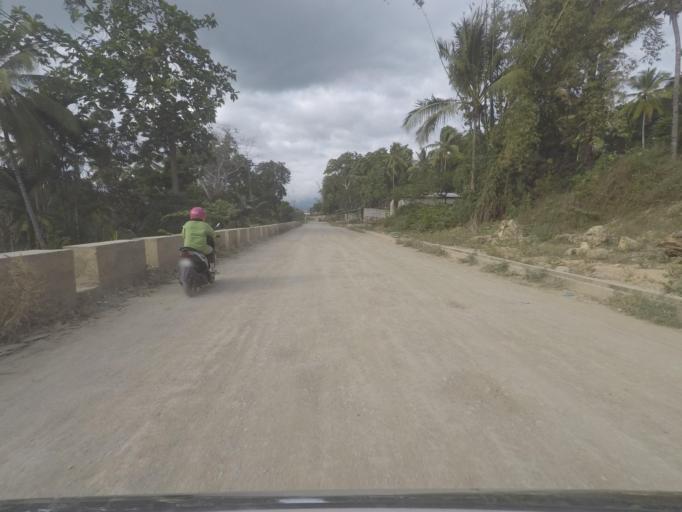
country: TL
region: Baucau
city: Venilale
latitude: -8.5893
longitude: 126.3869
